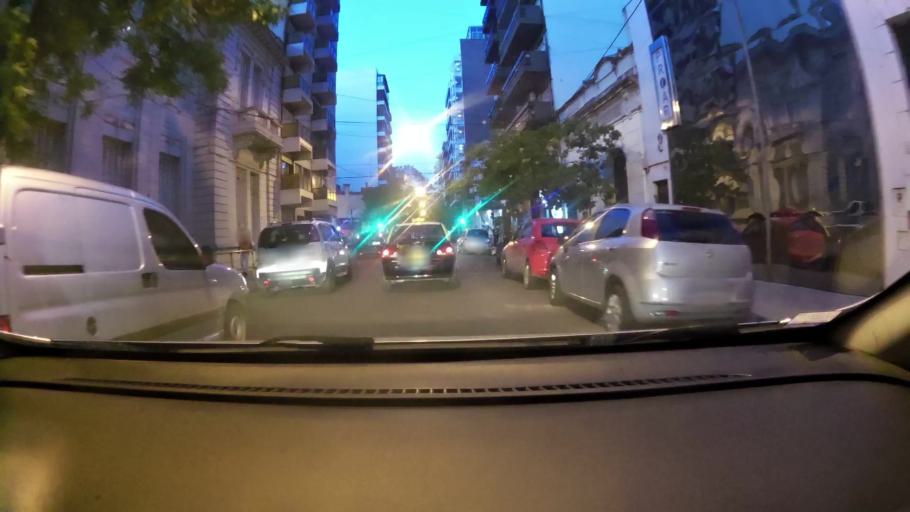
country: AR
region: Santa Fe
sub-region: Departamento de Rosario
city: Rosario
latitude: -32.9501
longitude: -60.6493
